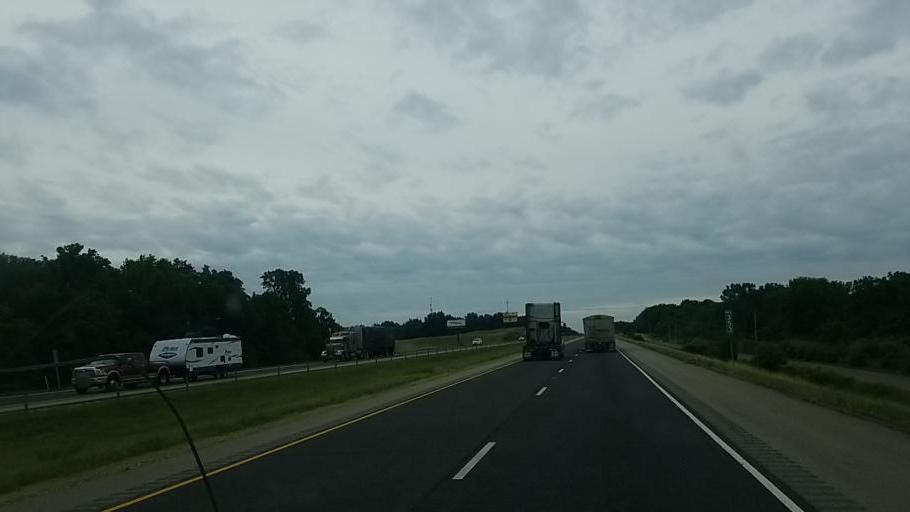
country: US
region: Indiana
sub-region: Steuben County
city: Angola
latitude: 41.6922
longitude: -85.0043
